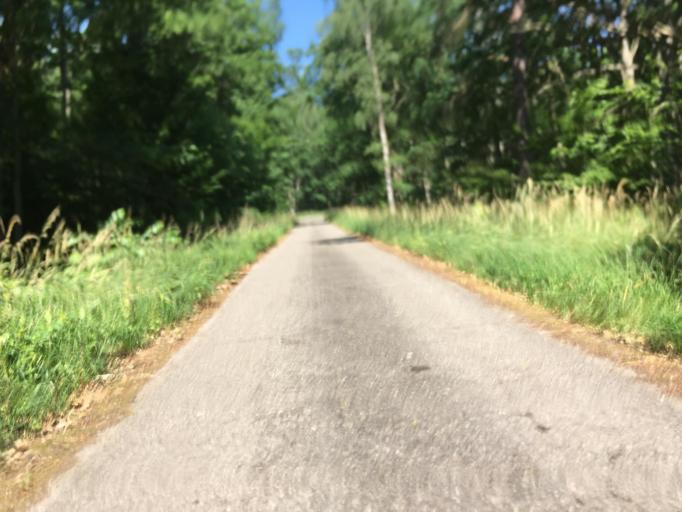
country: DE
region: Brandenburg
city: Marienwerder
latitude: 52.9154
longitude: 13.6652
